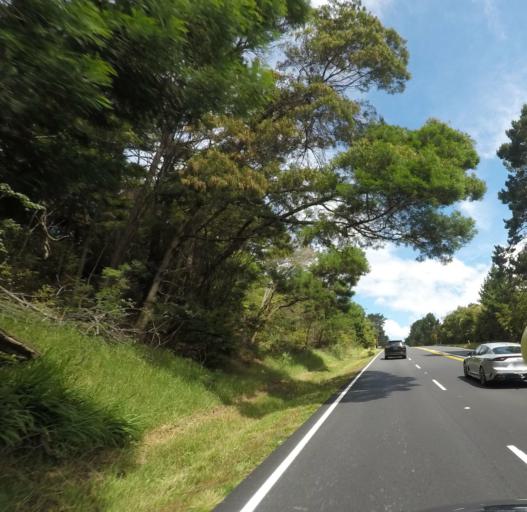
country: NZ
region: Auckland
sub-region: Auckland
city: Rothesay Bay
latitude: -36.6873
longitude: 174.7059
